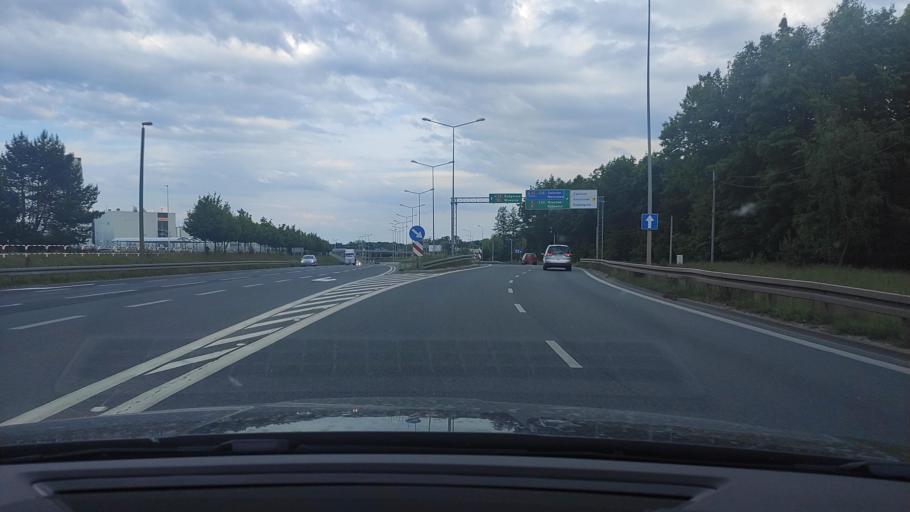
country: PL
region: Greater Poland Voivodeship
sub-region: Powiat poznanski
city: Kobylnica
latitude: 52.4156
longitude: 17.0226
